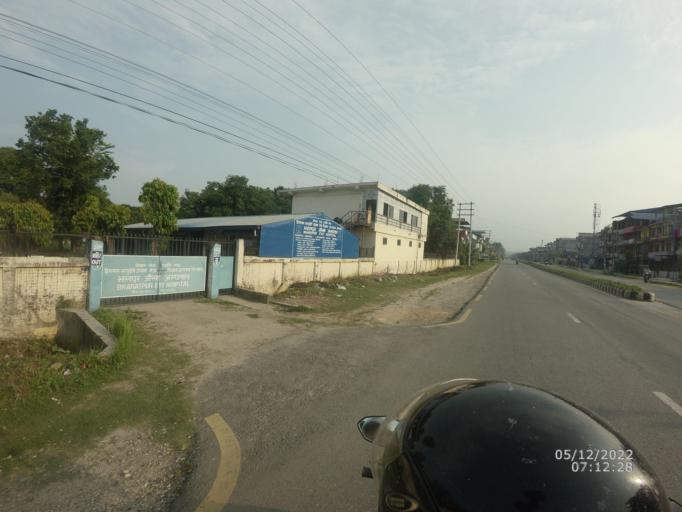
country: NP
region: Central Region
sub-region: Narayani Zone
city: Bharatpur
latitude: 27.6852
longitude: 84.4397
